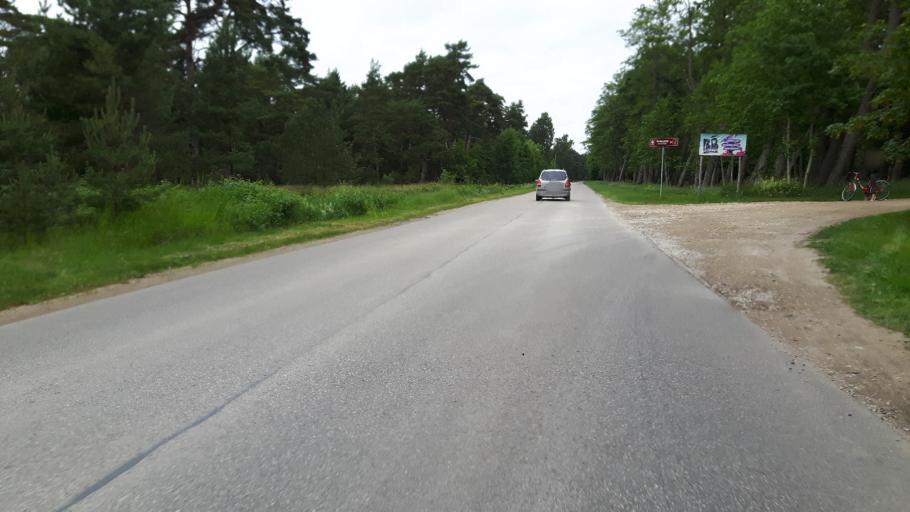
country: LV
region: Liepaja
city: Vec-Liepaja
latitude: 56.5634
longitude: 21.0146
